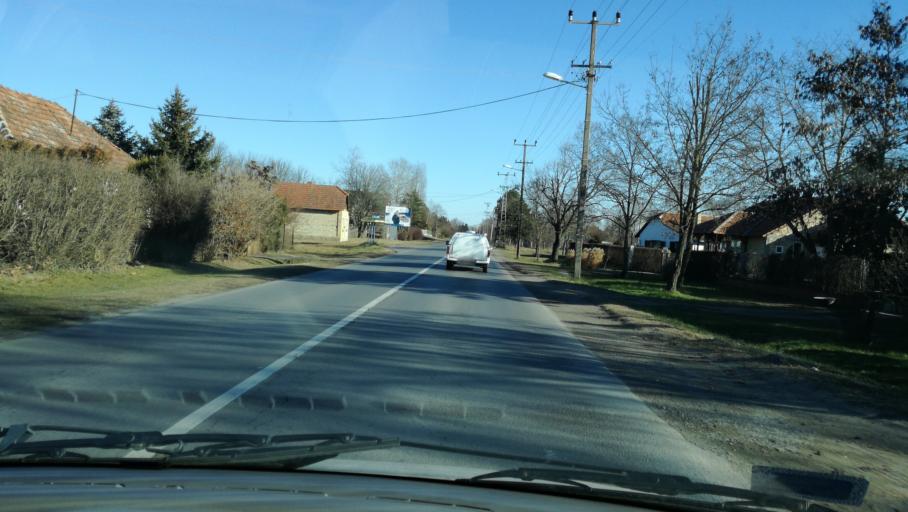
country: HU
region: Csongrad
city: Asotthalom
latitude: 46.1011
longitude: 19.7768
